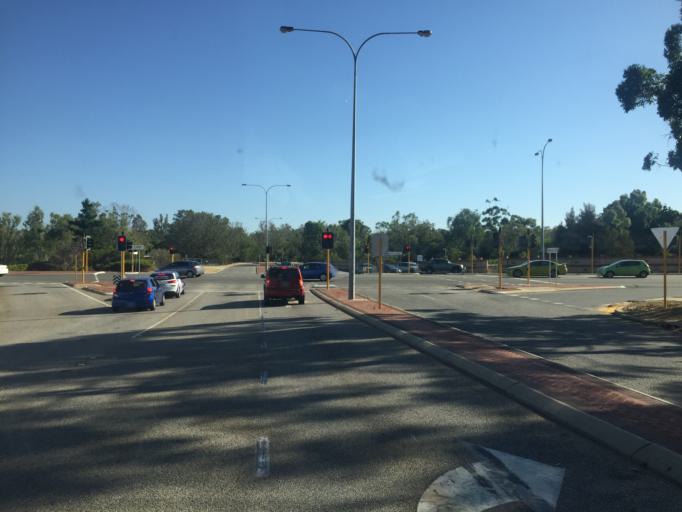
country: AU
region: Western Australia
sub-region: Gosnells
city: Kenwick
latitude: -32.0409
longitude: 115.9671
